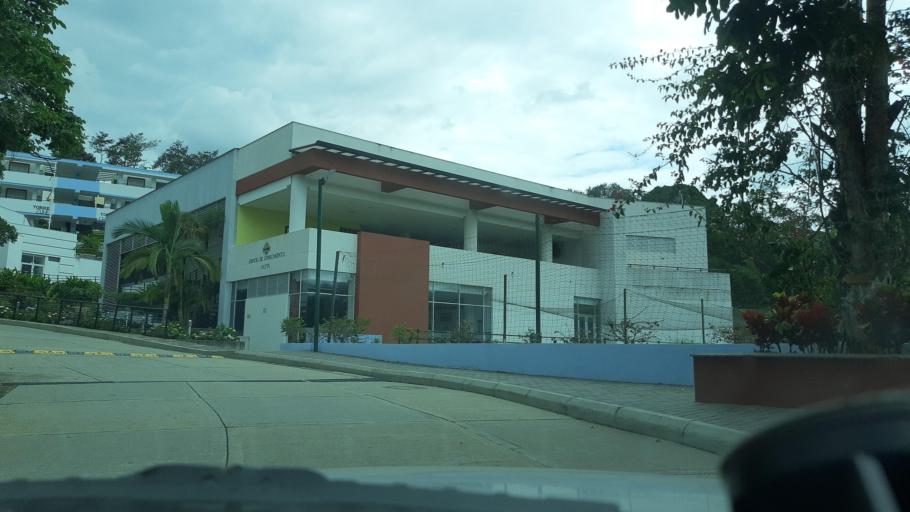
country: CO
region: Boyaca
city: Moniquira
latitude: 5.8817
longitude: -73.5779
